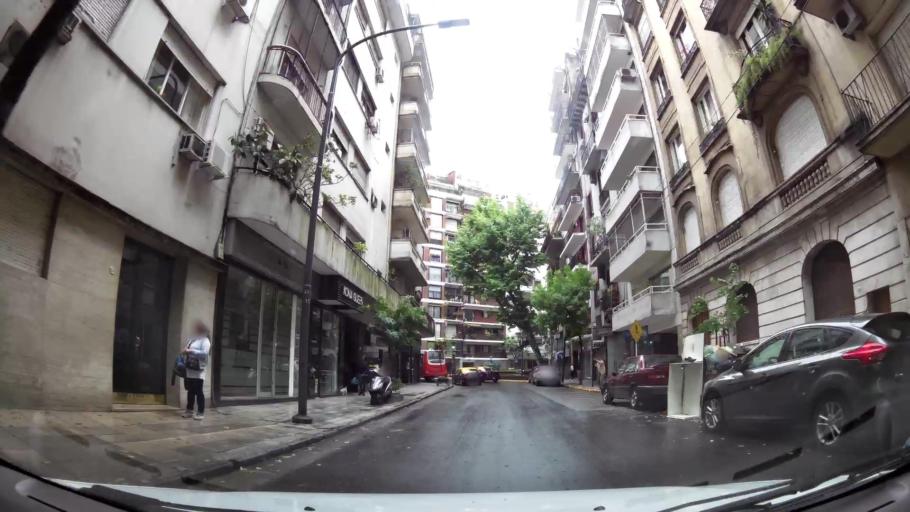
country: AR
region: Buenos Aires F.D.
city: Retiro
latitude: -34.5936
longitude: -58.3919
